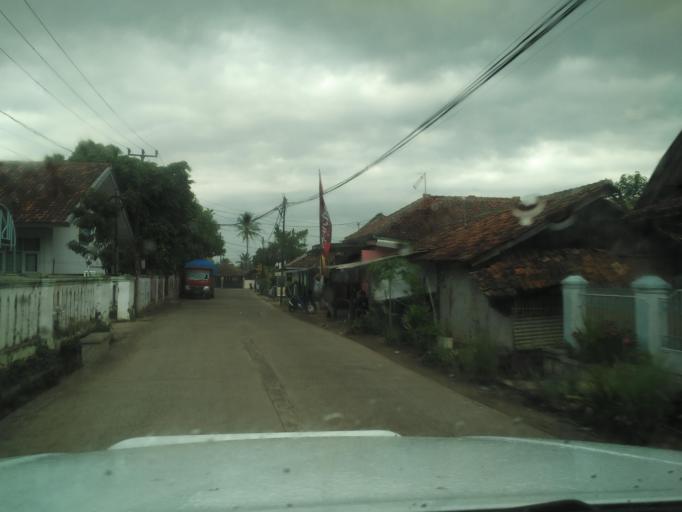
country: ID
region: West Java
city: Ciranjang-hilir
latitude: -6.7046
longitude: 107.1808
